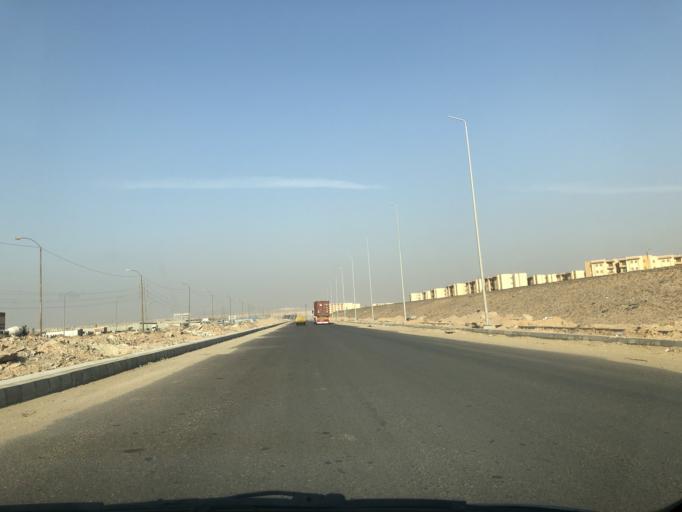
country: EG
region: Al Jizah
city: Madinat Sittah Uktubar
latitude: 29.9018
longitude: 30.9116
